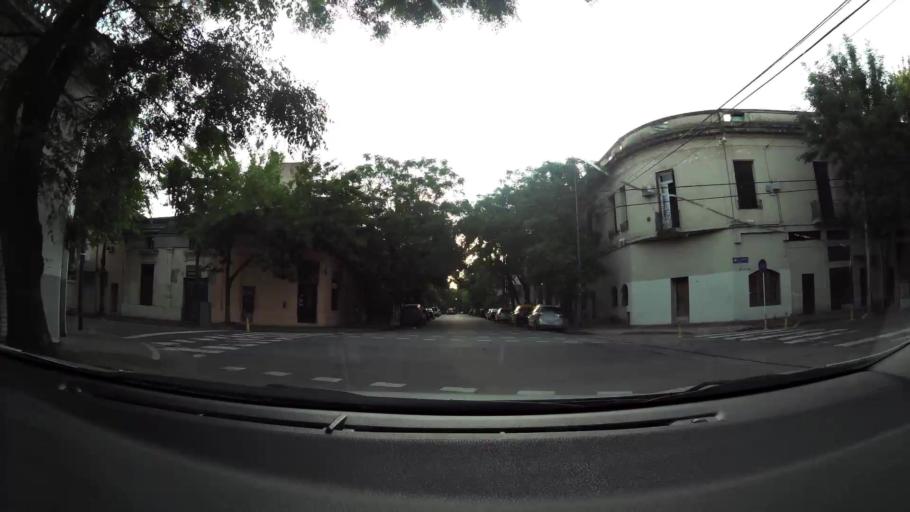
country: AR
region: Buenos Aires F.D.
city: Buenos Aires
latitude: -34.6332
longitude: -58.4129
